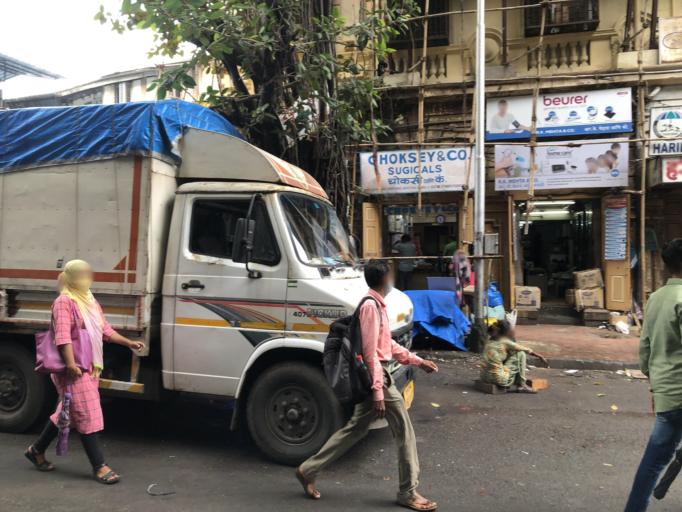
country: IN
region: Maharashtra
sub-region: Raigarh
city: Uran
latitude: 18.9476
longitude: 72.8309
